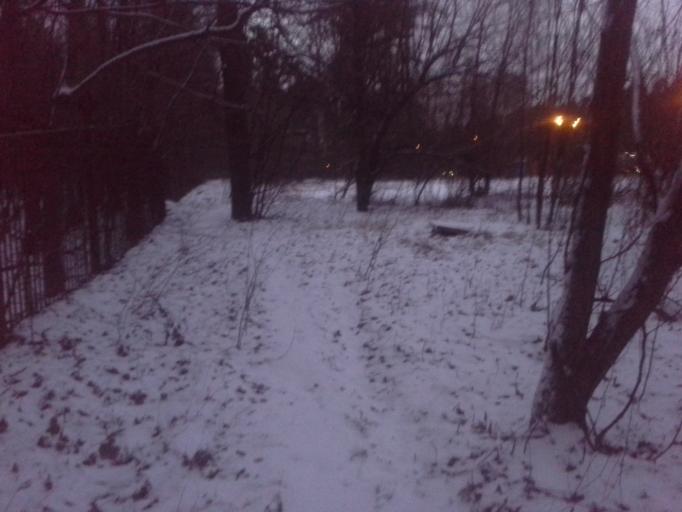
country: RU
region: Moscow
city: Chertanovo Yuzhnoye
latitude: 55.5838
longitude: 37.5562
